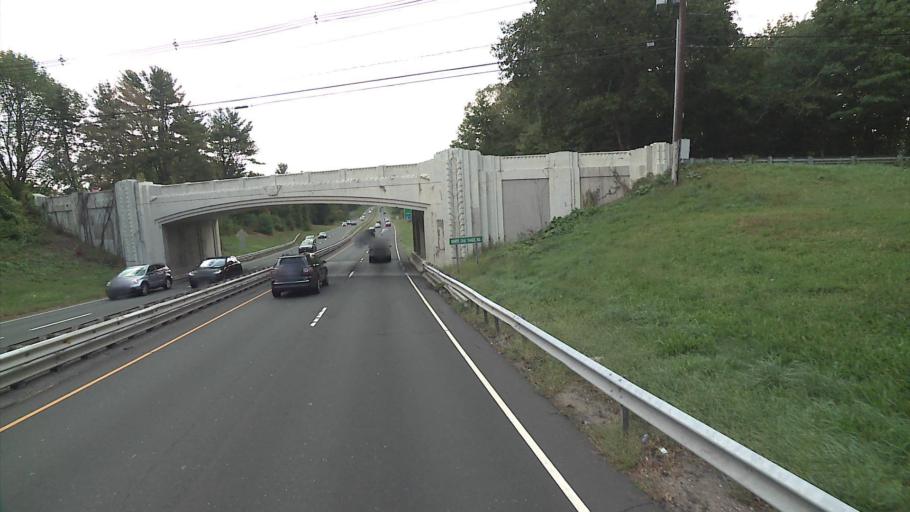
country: US
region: Connecticut
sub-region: Fairfield County
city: New Canaan
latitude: 41.1230
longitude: -73.4739
